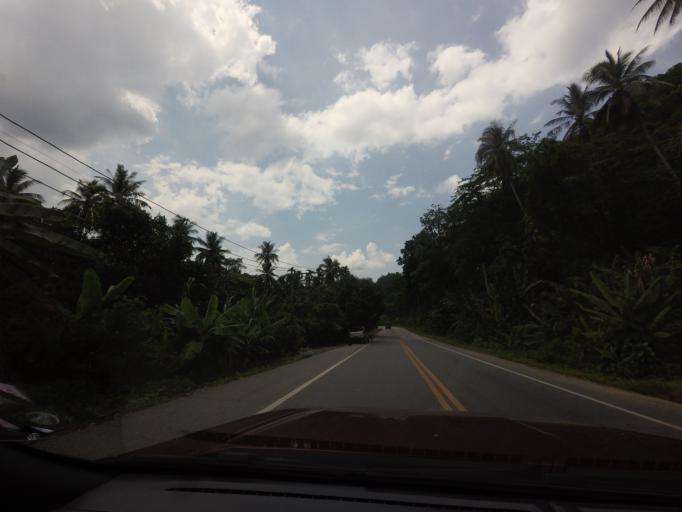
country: TH
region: Yala
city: Than To
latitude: 6.0659
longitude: 101.1967
